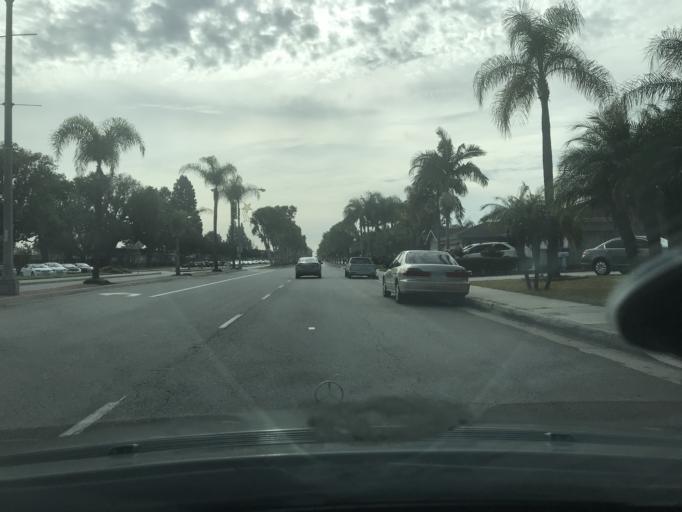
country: US
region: California
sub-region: Los Angeles County
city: Santa Fe Springs
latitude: 33.9426
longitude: -118.0907
